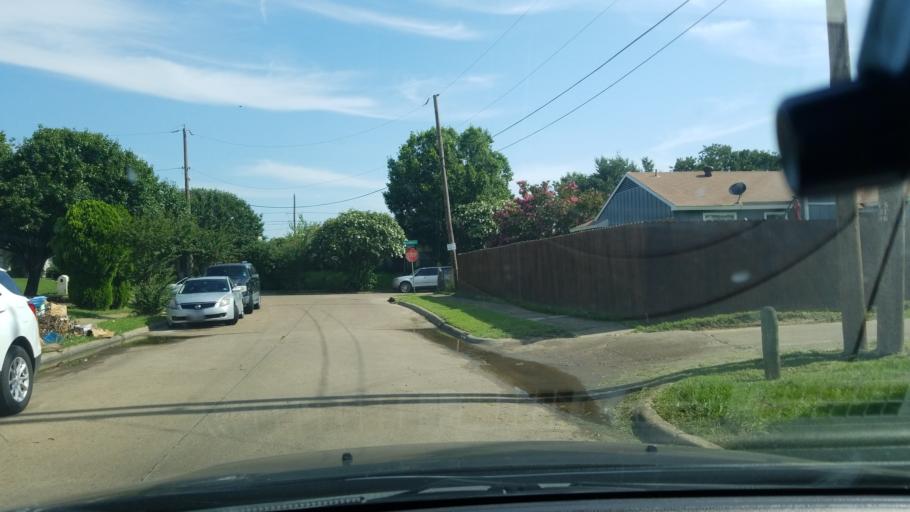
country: US
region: Texas
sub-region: Dallas County
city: Balch Springs
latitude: 32.7281
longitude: -96.6460
